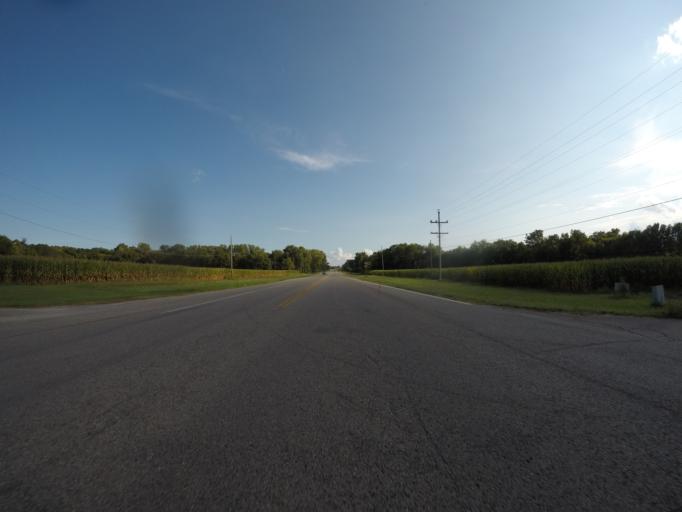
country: US
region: Kansas
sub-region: Shawnee County
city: Topeka
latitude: 39.1171
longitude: -95.5944
